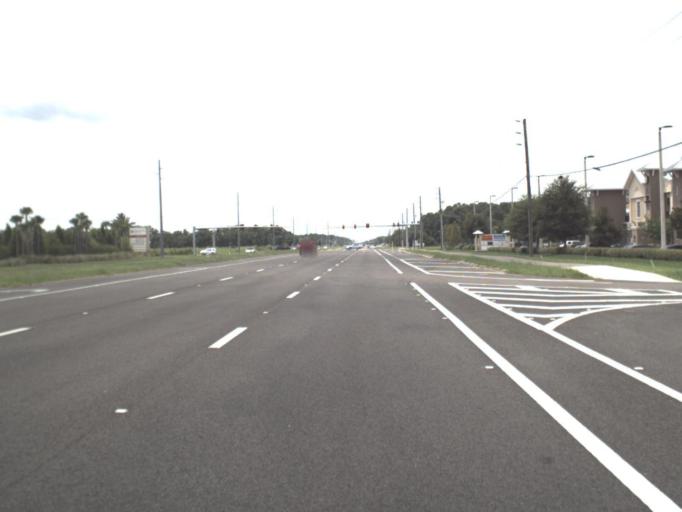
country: US
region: Florida
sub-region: Hillsborough County
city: Pebble Creek
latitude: 28.1961
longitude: -82.3537
